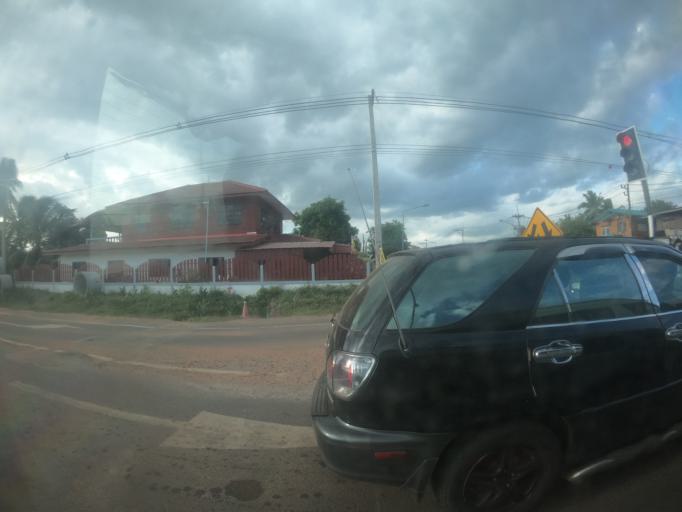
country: TH
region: Surin
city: Kap Choeng
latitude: 14.4557
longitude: 103.6801
